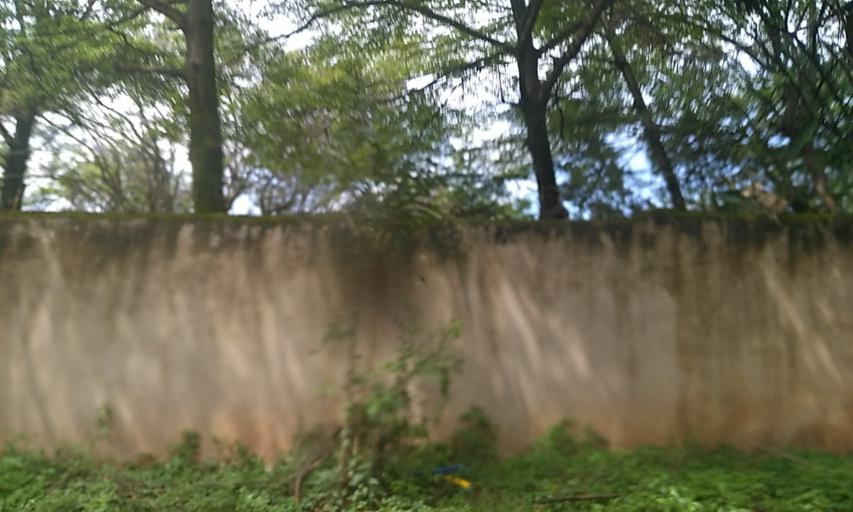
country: UG
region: Central Region
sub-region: Kampala District
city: Kampala
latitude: 0.3308
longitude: 32.6003
